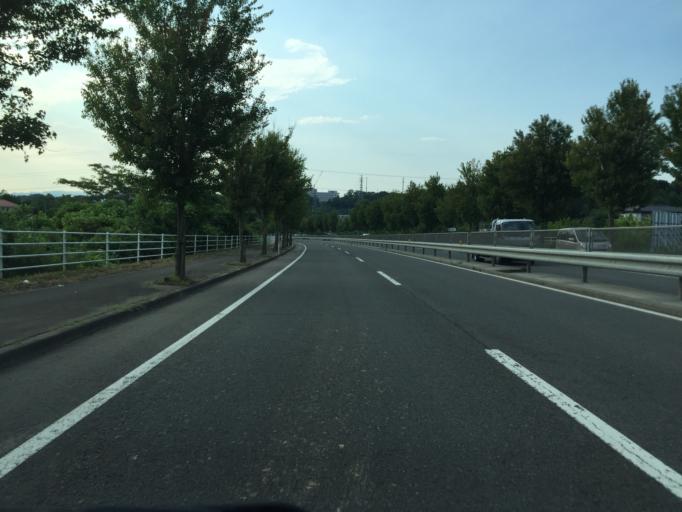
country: JP
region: Fukushima
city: Fukushima-shi
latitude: 37.6796
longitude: 140.4768
